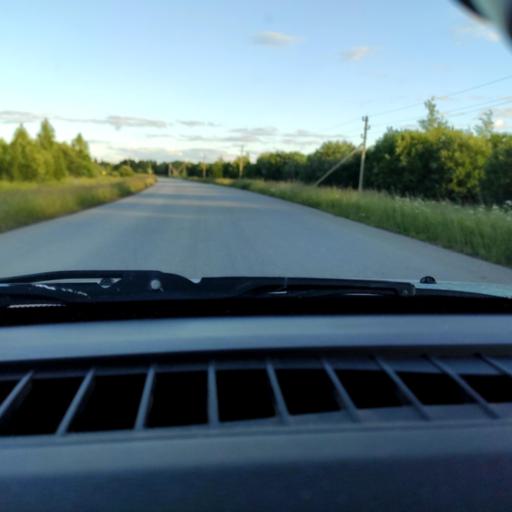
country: RU
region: Perm
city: Polazna
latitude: 58.2010
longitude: 56.5318
